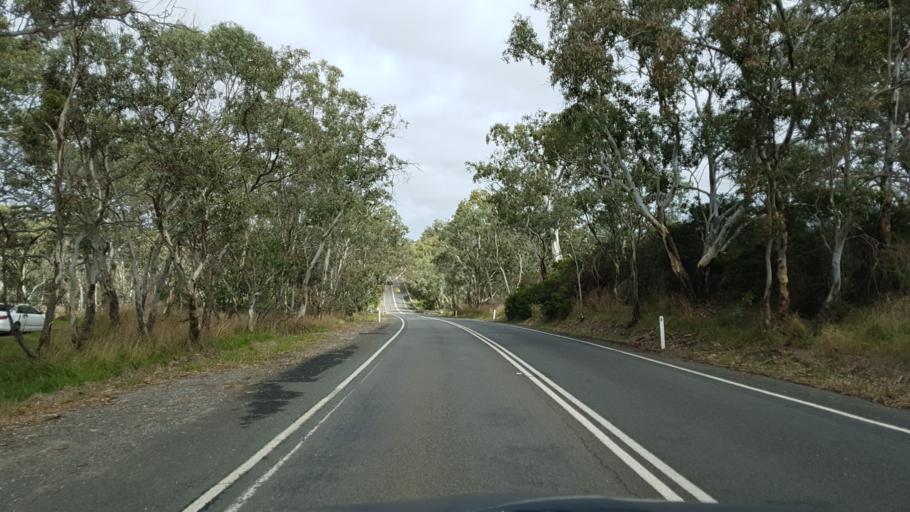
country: AU
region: South Australia
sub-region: Mount Barker
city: Nairne
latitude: -35.0414
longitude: 138.9329
